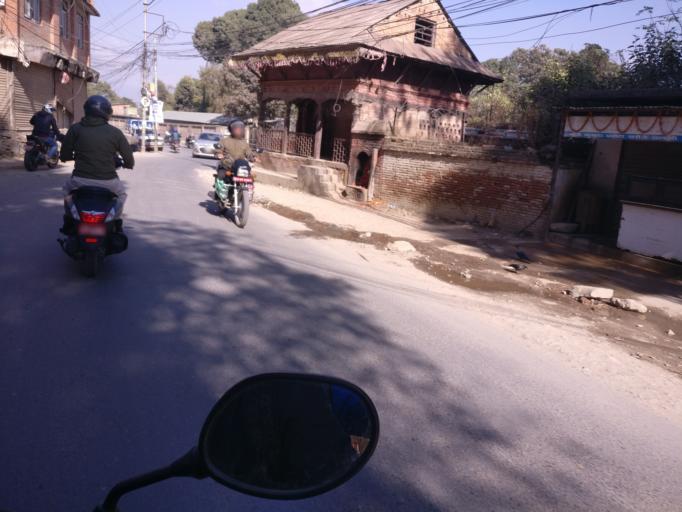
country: NP
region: Central Region
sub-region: Bagmati Zone
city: Patan
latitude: 27.6631
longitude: 85.3195
